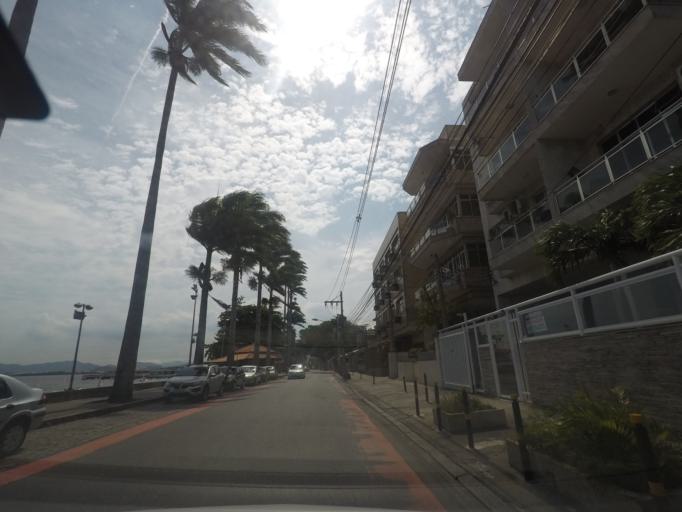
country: BR
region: Rio de Janeiro
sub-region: Rio De Janeiro
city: Rio de Janeiro
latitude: -22.8187
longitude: -43.1988
